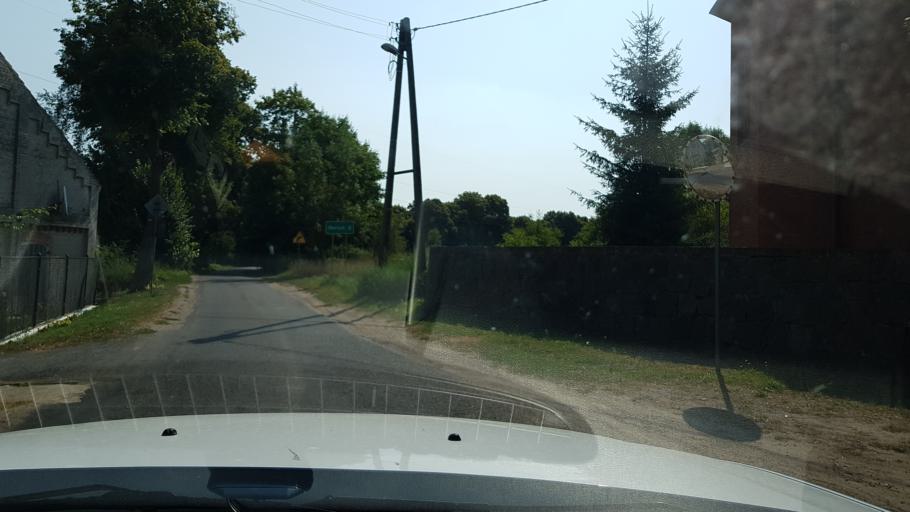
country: PL
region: West Pomeranian Voivodeship
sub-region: Powiat gryfinski
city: Chojna
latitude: 52.9516
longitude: 14.5060
